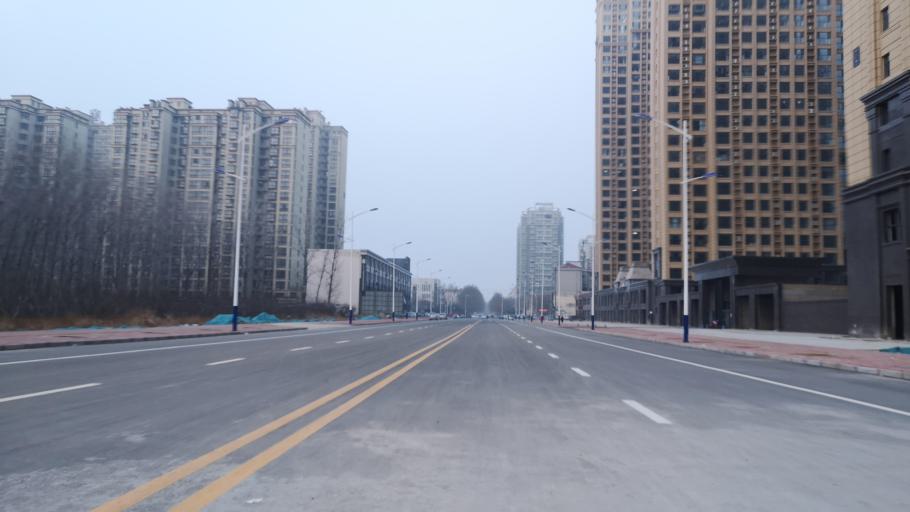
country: CN
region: Henan Sheng
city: Zhongyuanlu
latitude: 35.7506
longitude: 115.0601
